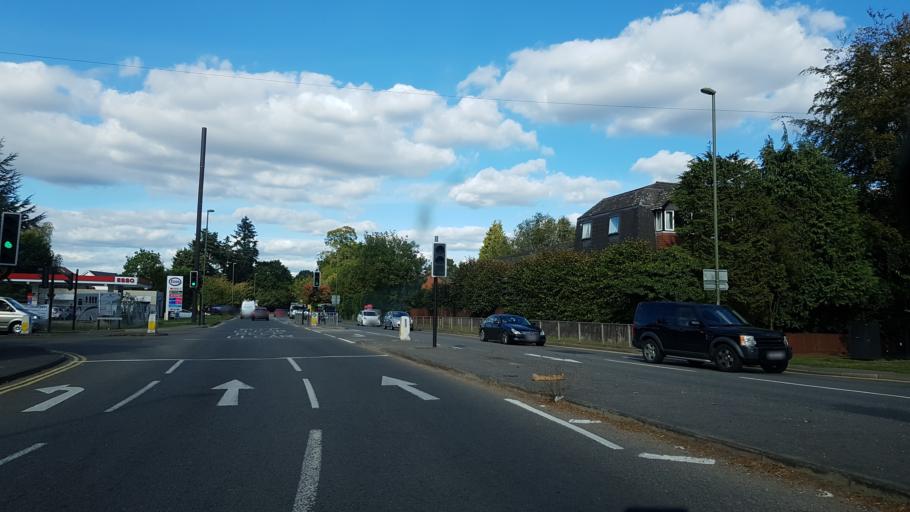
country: GB
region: England
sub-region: Surrey
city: Milford
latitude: 51.1727
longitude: -0.6506
